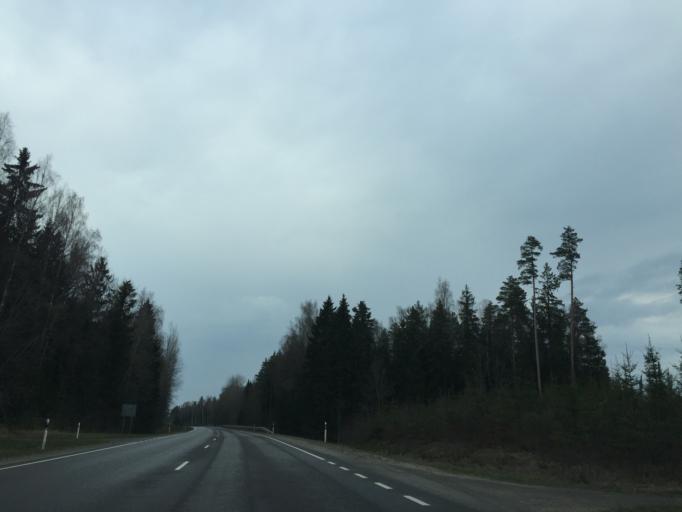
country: EE
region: Tartu
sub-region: UElenurme vald
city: Ulenurme
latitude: 58.1021
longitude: 26.7404
